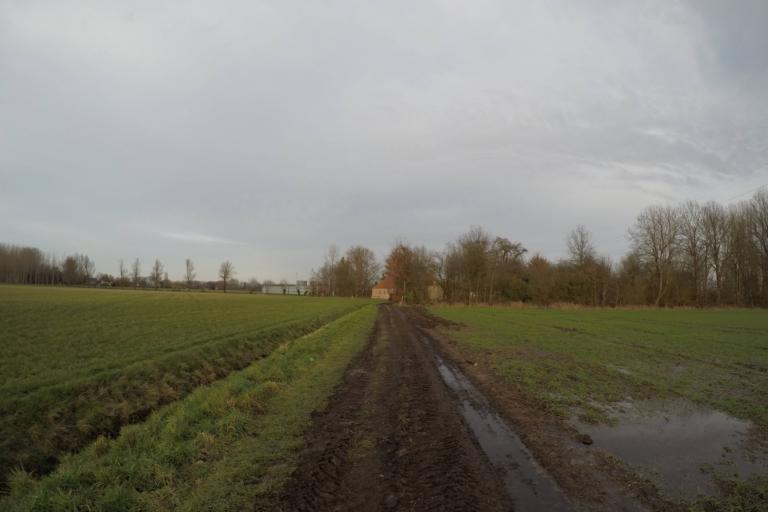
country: BE
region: Flanders
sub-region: Provincie Antwerpen
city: Ranst
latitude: 51.1923
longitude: 4.5740
